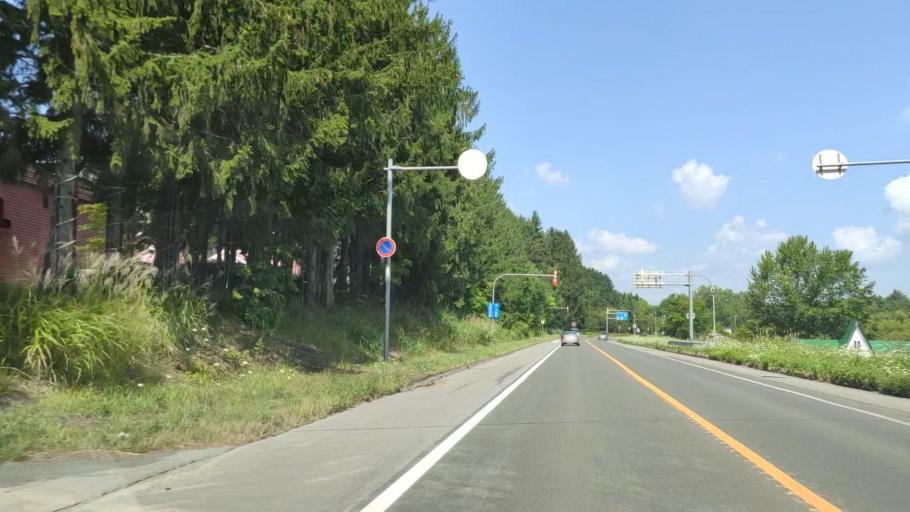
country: JP
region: Hokkaido
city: Shimo-furano
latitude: 43.5132
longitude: 142.4484
